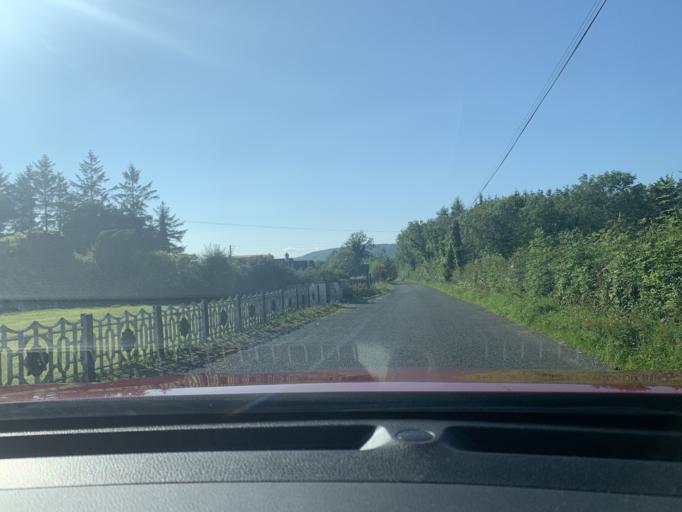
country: IE
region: Connaught
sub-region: Sligo
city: Tobercurry
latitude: 54.0741
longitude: -8.7805
